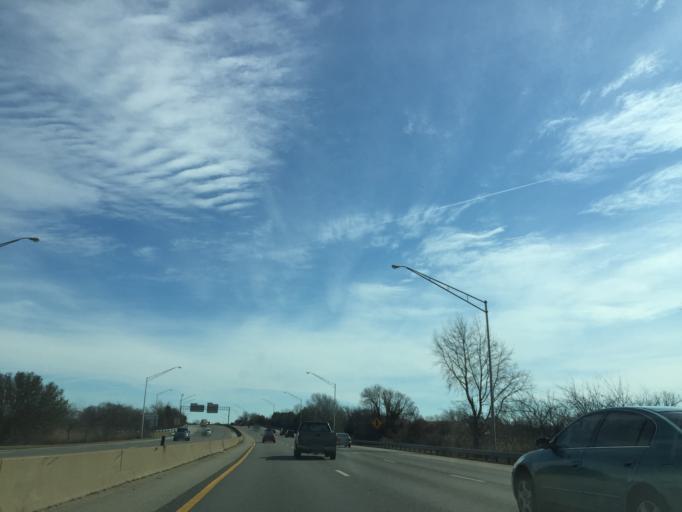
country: US
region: Virginia
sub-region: City of Hampton
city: Hampton
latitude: 37.0323
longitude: -76.3667
